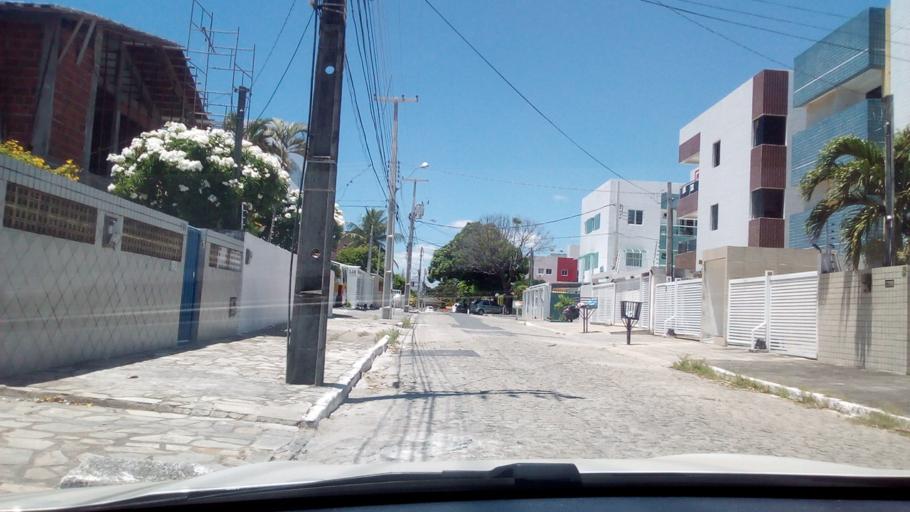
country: BR
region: Paraiba
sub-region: Joao Pessoa
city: Joao Pessoa
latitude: -7.1457
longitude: -34.8411
